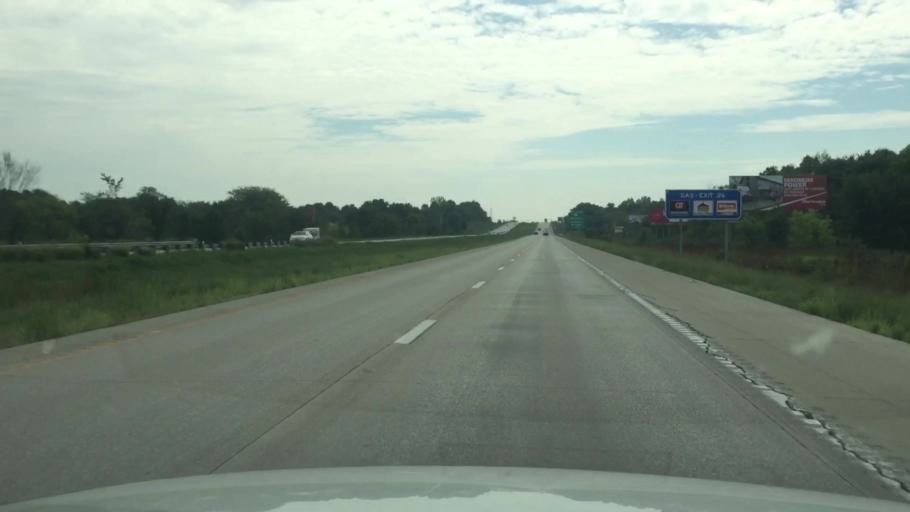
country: US
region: Missouri
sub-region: Clay County
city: Kearney
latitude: 39.3883
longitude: -94.3615
